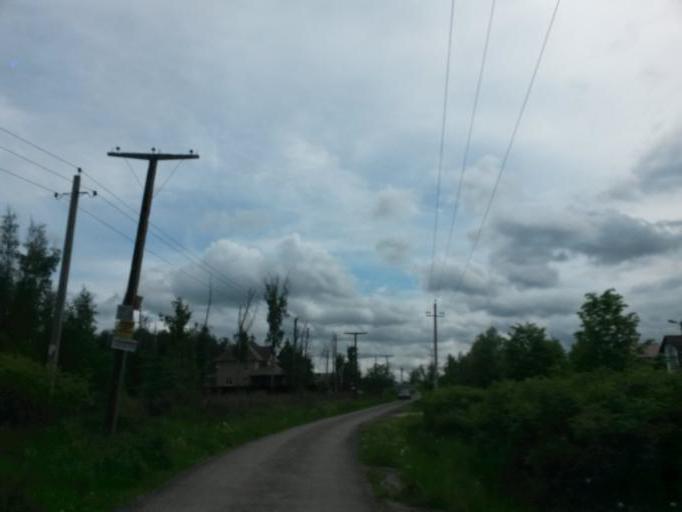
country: RU
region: Moskovskaya
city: Lyubuchany
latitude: 55.2708
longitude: 37.6256
